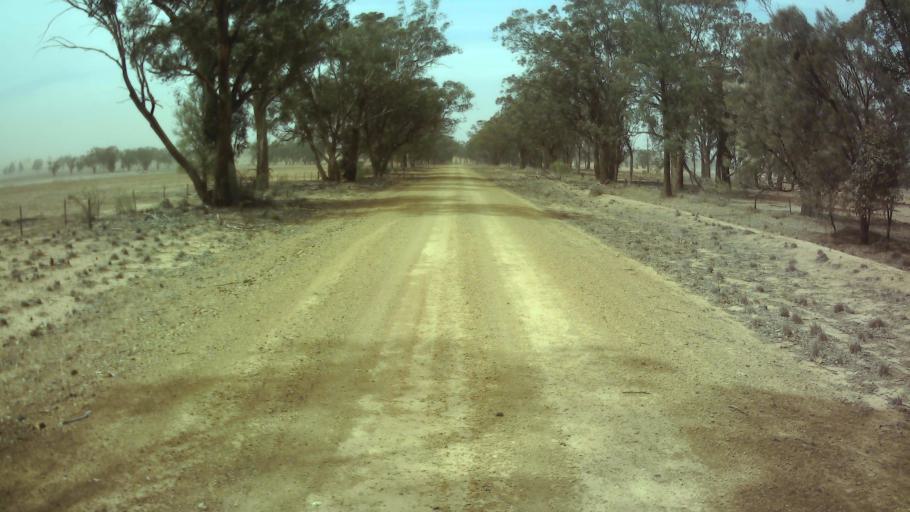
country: AU
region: New South Wales
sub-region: Weddin
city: Grenfell
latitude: -33.7368
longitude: 147.9617
